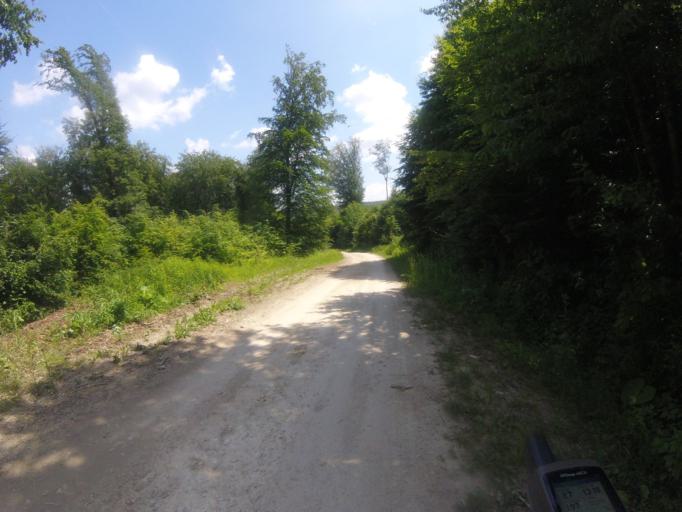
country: HU
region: Veszprem
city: Cseteny
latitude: 47.2685
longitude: 17.9935
